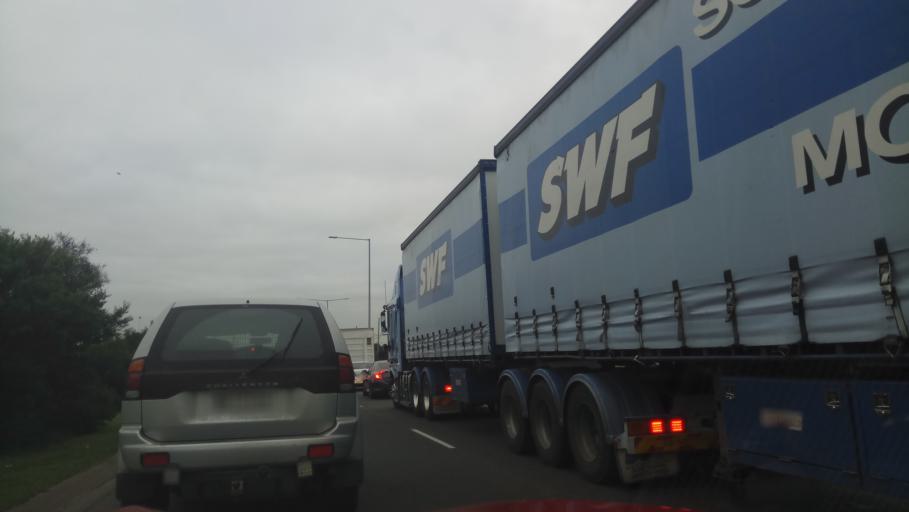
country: AU
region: Victoria
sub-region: Hobsons Bay
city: Altona North
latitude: -37.8433
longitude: 144.8250
